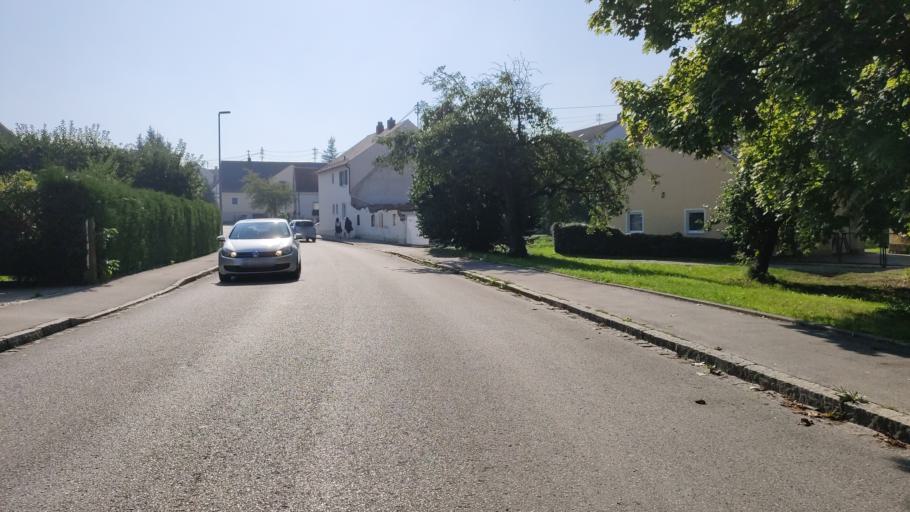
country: DE
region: Bavaria
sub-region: Swabia
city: Bobingen
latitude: 48.2727
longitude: 10.8325
